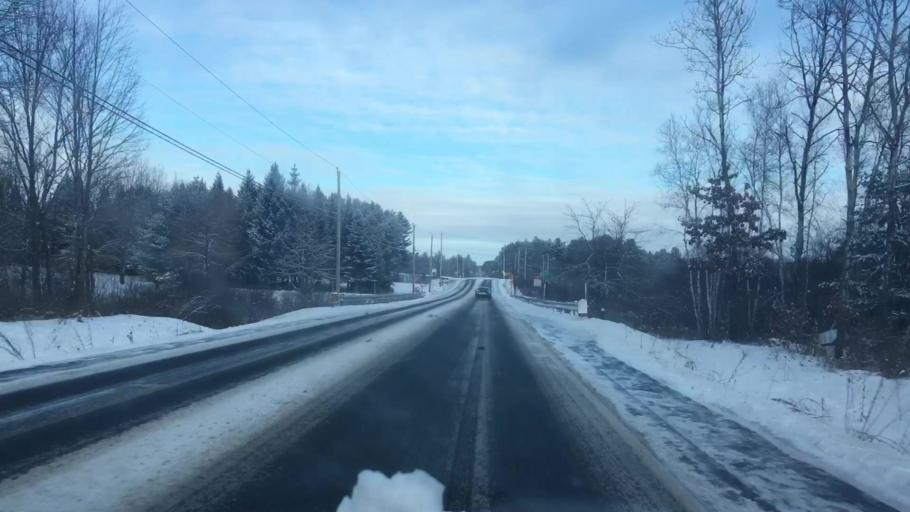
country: US
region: Maine
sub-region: Cumberland County
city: North Windham
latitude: 43.7959
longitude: -70.4400
